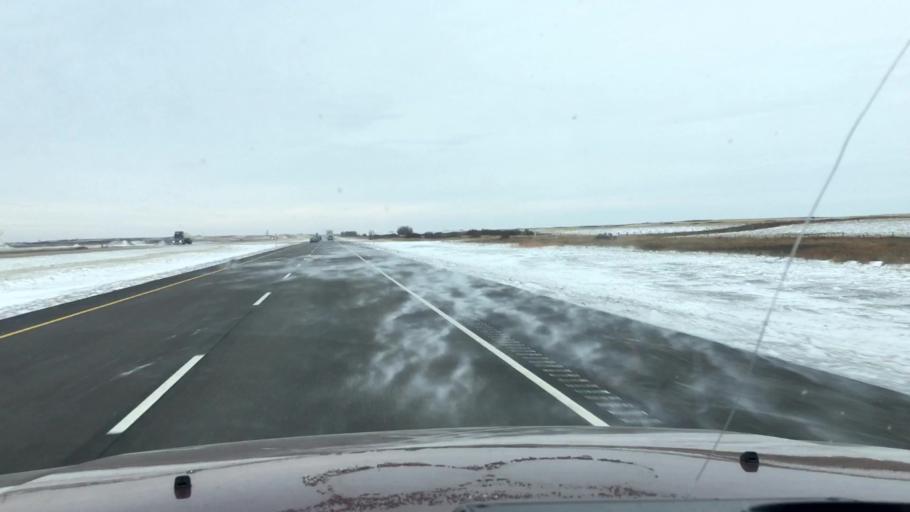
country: CA
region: Saskatchewan
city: Moose Jaw
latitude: 50.8940
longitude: -105.6284
